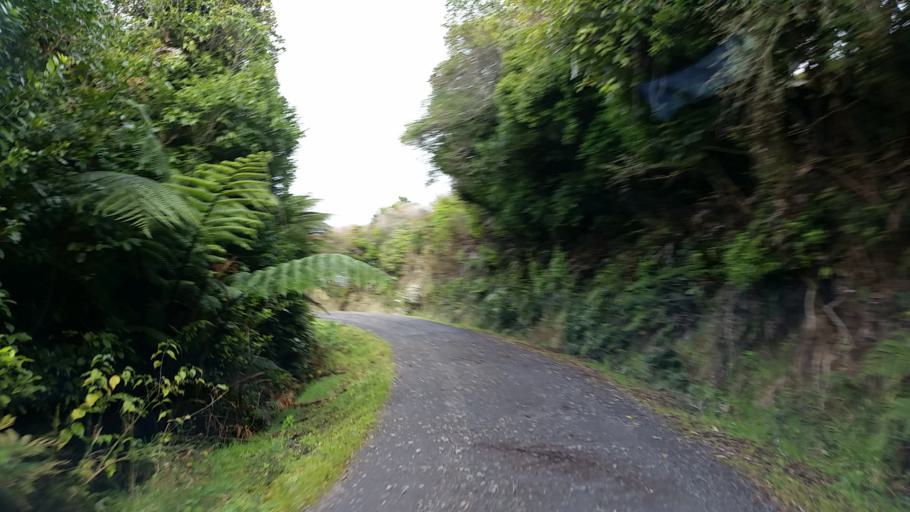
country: NZ
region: Taranaki
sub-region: South Taranaki District
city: Eltham
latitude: -39.4076
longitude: 174.5700
